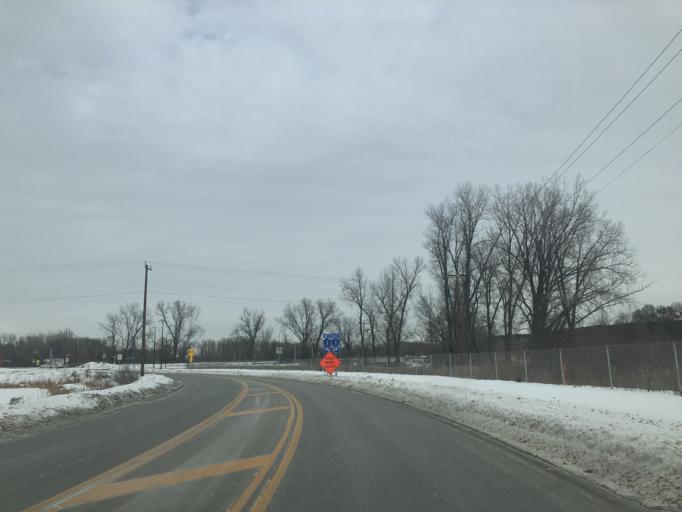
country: US
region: Minnesota
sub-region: Ramsey County
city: Mounds View
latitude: 45.1065
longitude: -93.1864
